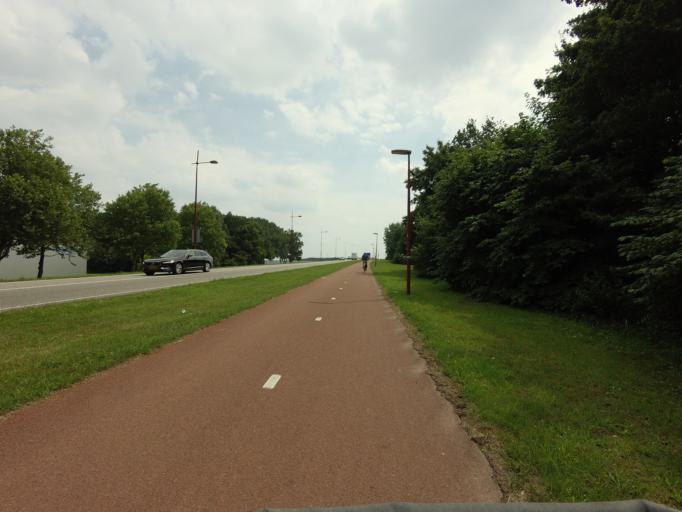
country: NL
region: Utrecht
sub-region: Gemeente Vianen
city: Vianen
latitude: 52.0158
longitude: 5.1068
